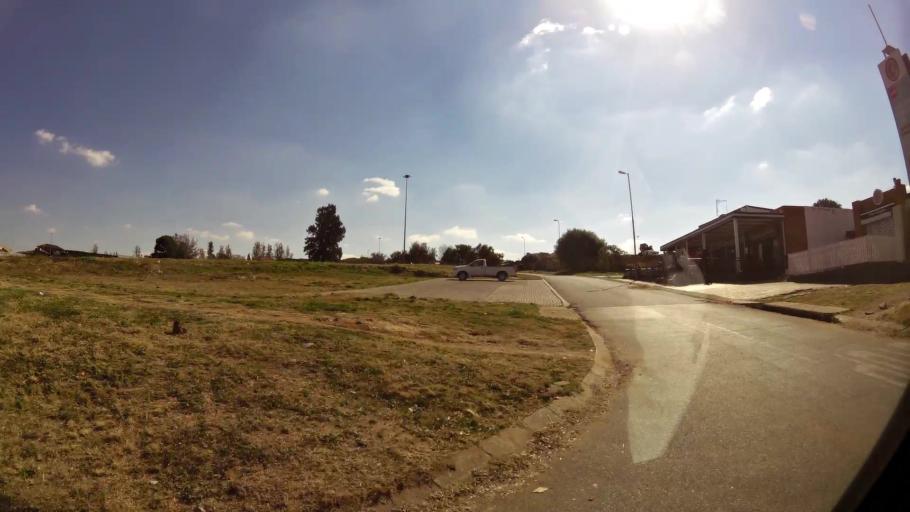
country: ZA
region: Gauteng
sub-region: City of Johannesburg Metropolitan Municipality
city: Soweto
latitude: -26.2444
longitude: 27.9054
